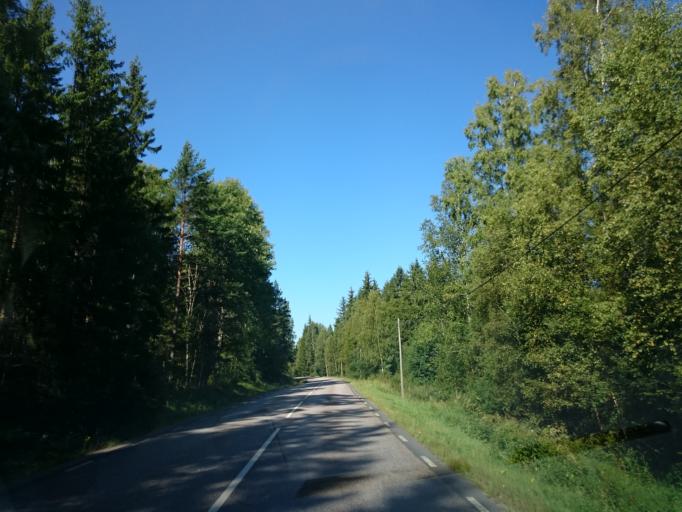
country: SE
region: OEstergoetland
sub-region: Norrkopings Kommun
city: Krokek
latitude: 58.6585
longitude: 16.5169
